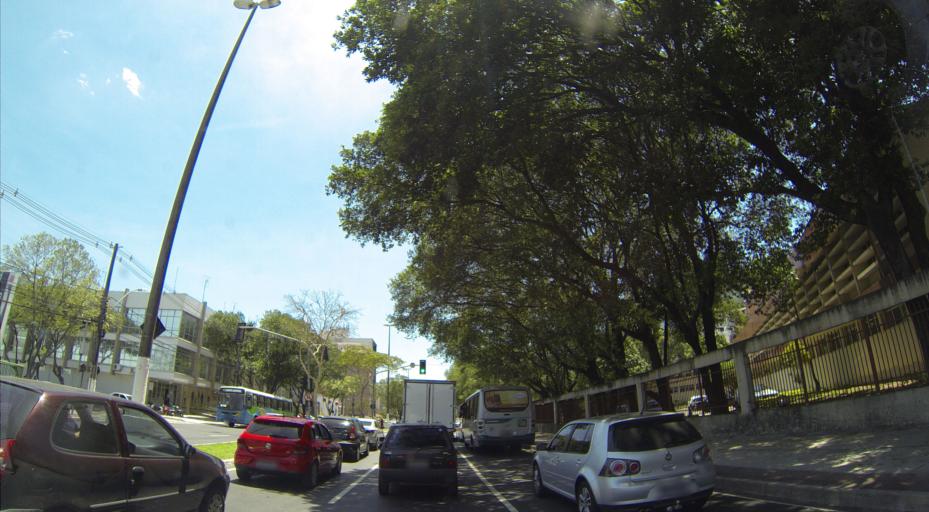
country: BR
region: Espirito Santo
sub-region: Vila Velha
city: Vila Velha
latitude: -20.3179
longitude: -40.3062
